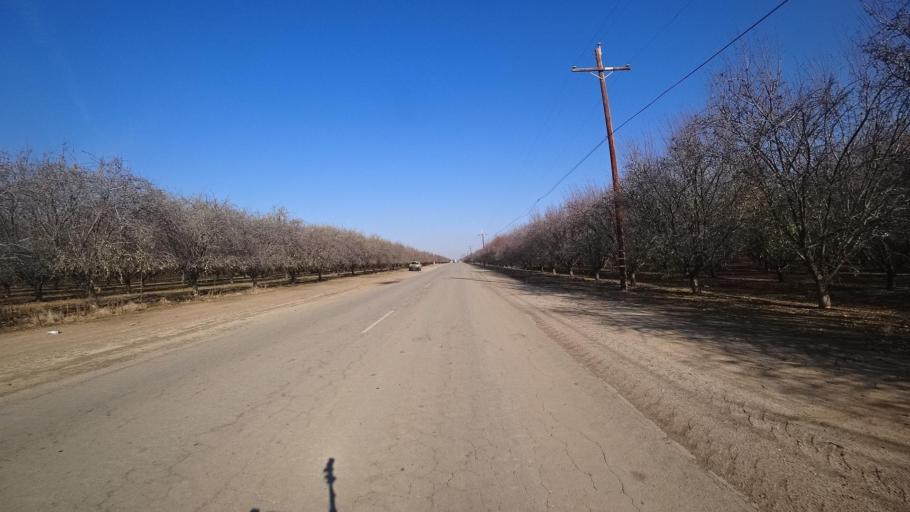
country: US
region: California
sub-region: Kern County
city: Weedpatch
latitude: 35.2035
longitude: -118.8961
